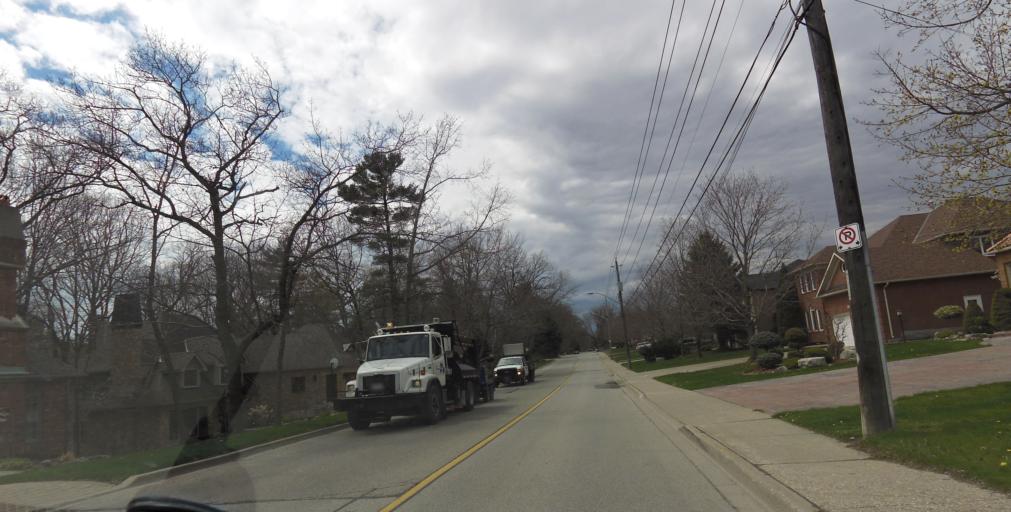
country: CA
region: Ontario
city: Mississauga
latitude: 43.5587
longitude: -79.6103
